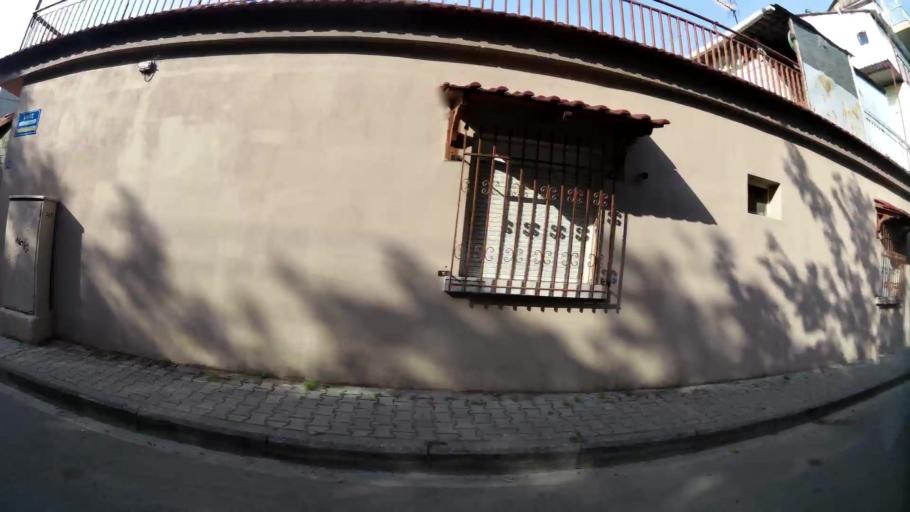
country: GR
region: Central Macedonia
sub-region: Nomos Thessalonikis
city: Menemeni
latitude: 40.6578
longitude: 22.9085
